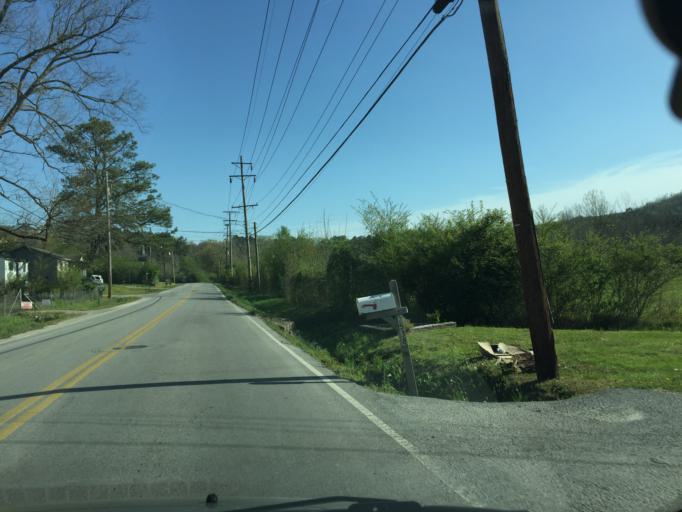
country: US
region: Tennessee
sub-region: Hamilton County
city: East Chattanooga
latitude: 35.0622
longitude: -85.2286
